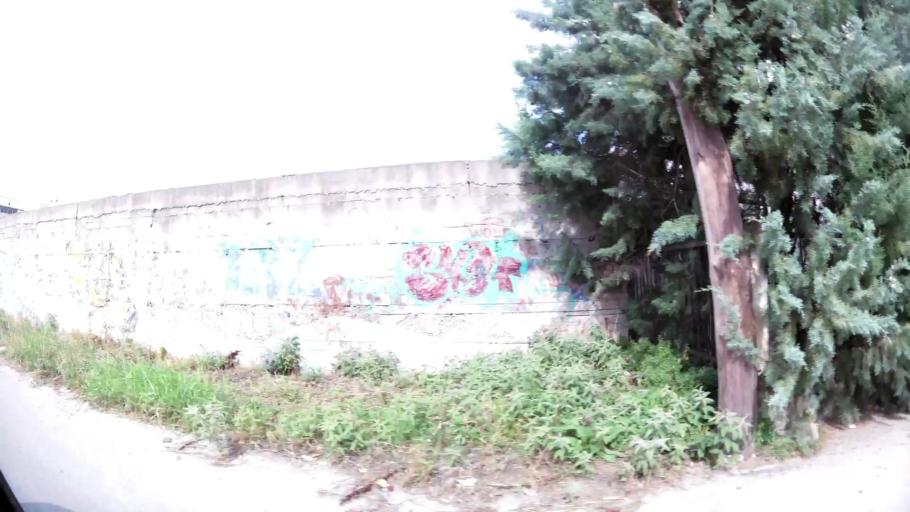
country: GR
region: Central Macedonia
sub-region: Nomos Thessalonikis
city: Stavroupoli
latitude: 40.6900
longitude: 22.9294
